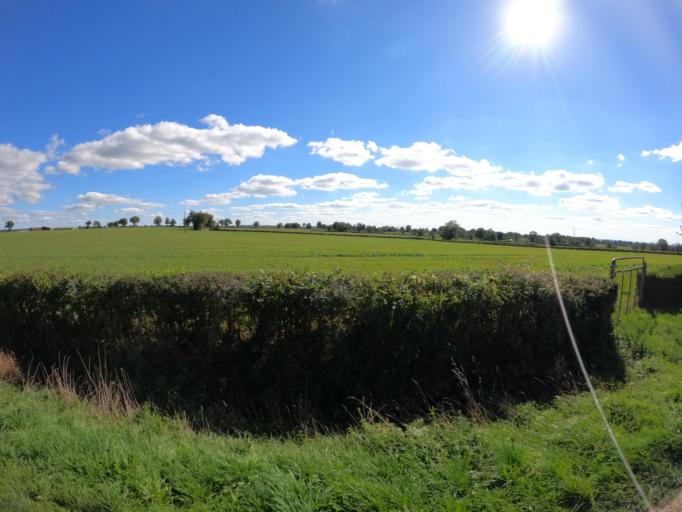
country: FR
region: Auvergne
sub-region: Departement de l'Allier
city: Buxieres-les-Mines
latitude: 46.4031
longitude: 2.9773
